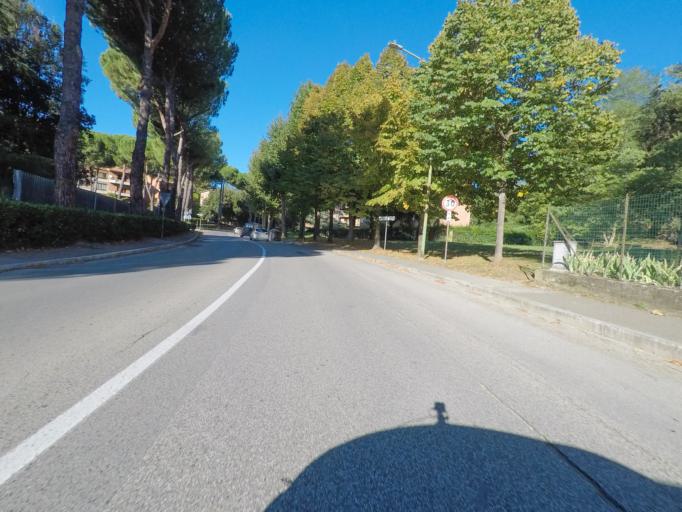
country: IT
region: Tuscany
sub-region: Provincia di Siena
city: Belverde
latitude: 43.3387
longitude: 11.3003
